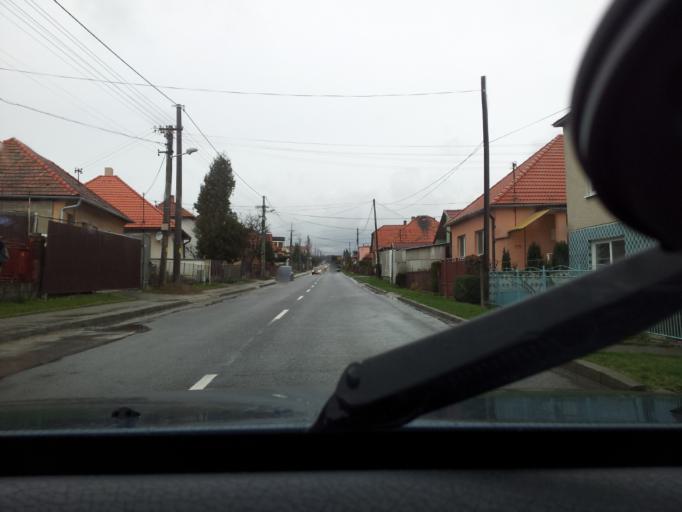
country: SK
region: Nitriansky
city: Tlmace
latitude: 48.3209
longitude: 18.5177
